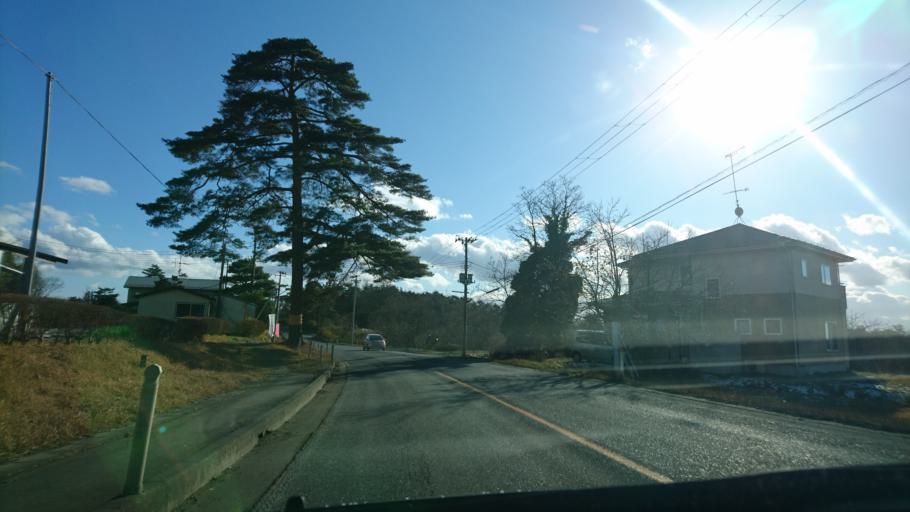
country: JP
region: Iwate
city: Ichinoseki
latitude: 38.7954
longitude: 141.2093
